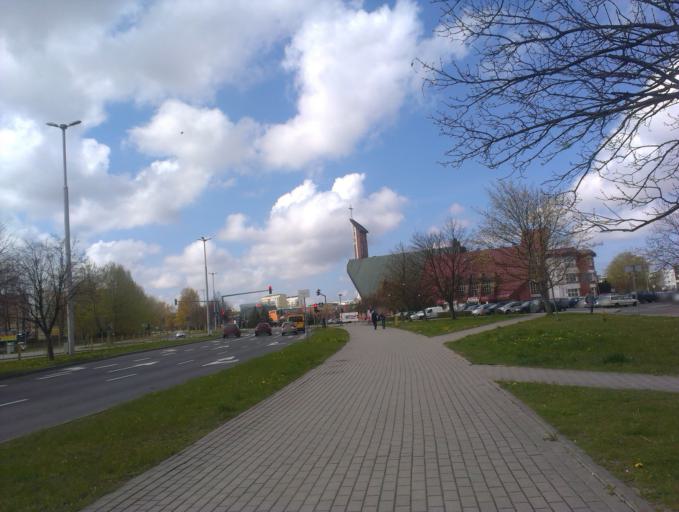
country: PL
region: West Pomeranian Voivodeship
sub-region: Koszalin
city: Koszalin
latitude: 54.2053
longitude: 16.1928
